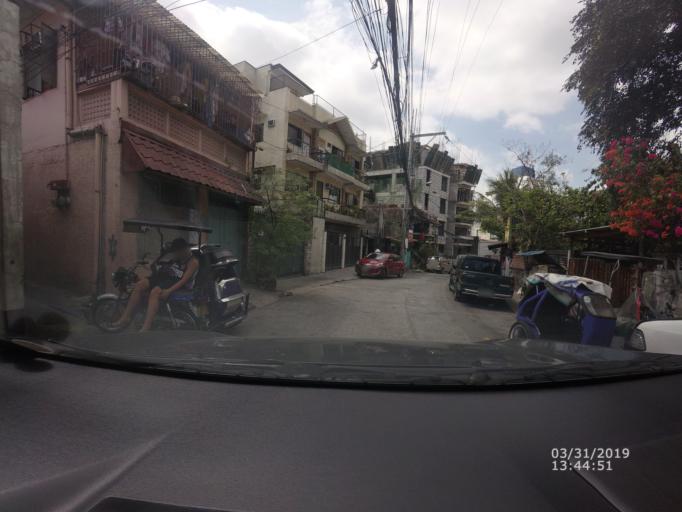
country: PH
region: Metro Manila
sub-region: Mandaluyong
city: Mandaluyong City
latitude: 14.5821
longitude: 121.0473
